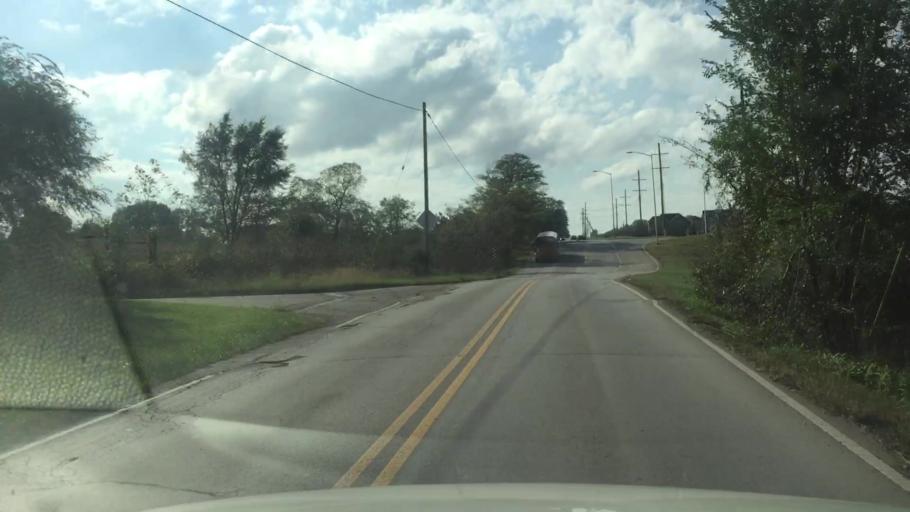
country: US
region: Kansas
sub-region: Johnson County
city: Lenexa
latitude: 38.8255
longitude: -94.6792
